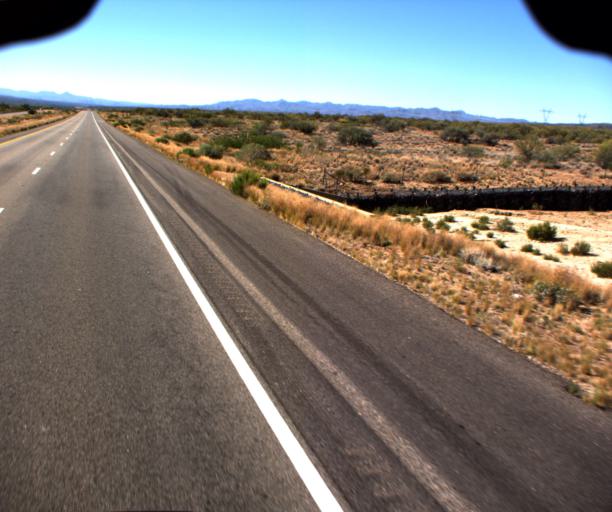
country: US
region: Arizona
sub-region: Mohave County
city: Kingman
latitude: 34.8787
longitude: -113.6477
